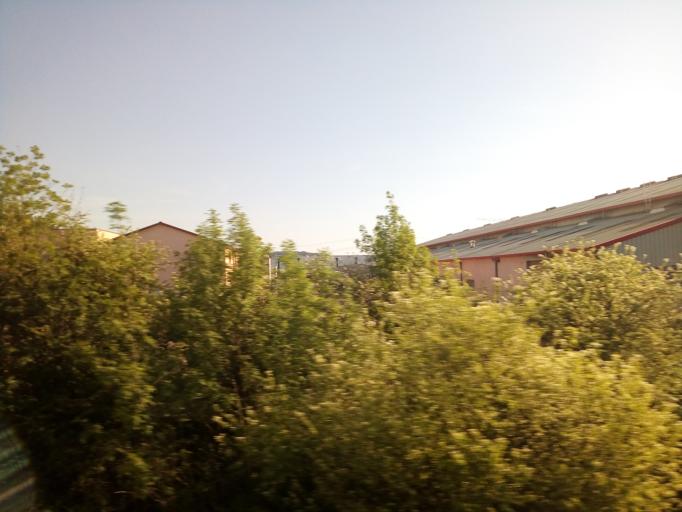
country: FR
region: Rhone-Alpes
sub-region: Departement du Rhone
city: Saint-Pierre-de-Chandieu
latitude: 45.6674
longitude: 5.0120
